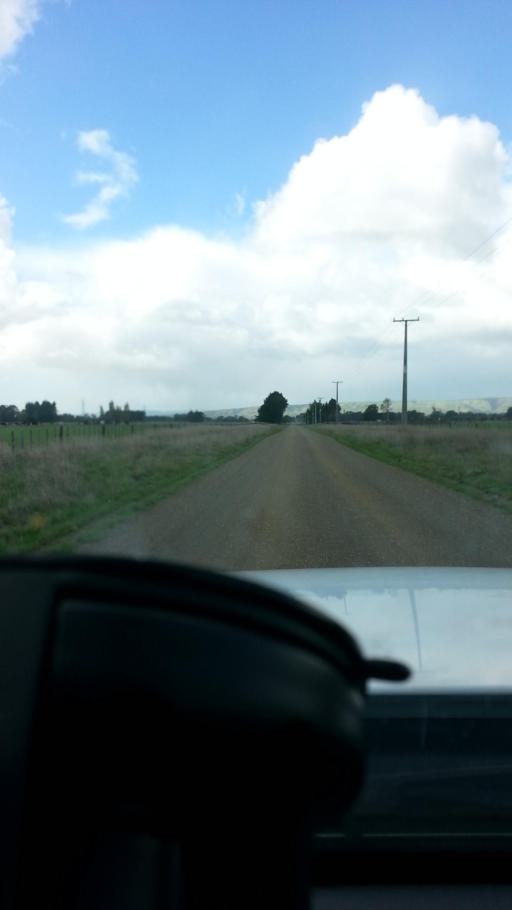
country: NZ
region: Wellington
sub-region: Masterton District
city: Masterton
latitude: -41.1187
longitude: 175.4058
